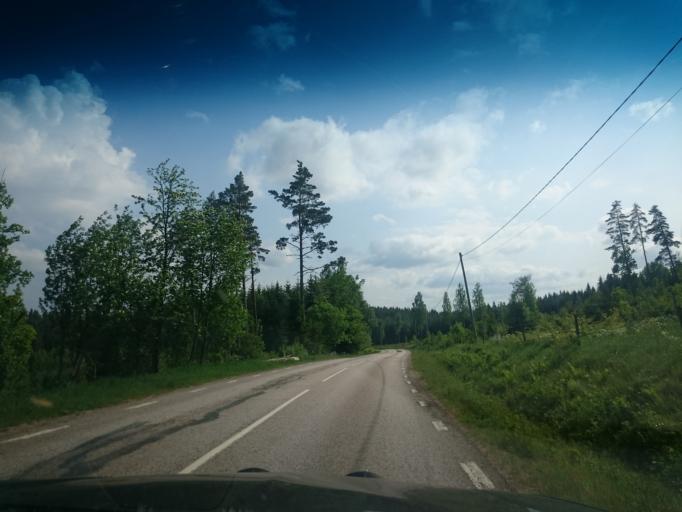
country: SE
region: Joenkoeping
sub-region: Vetlanda Kommun
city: Vetlanda
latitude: 57.3402
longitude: 15.0761
